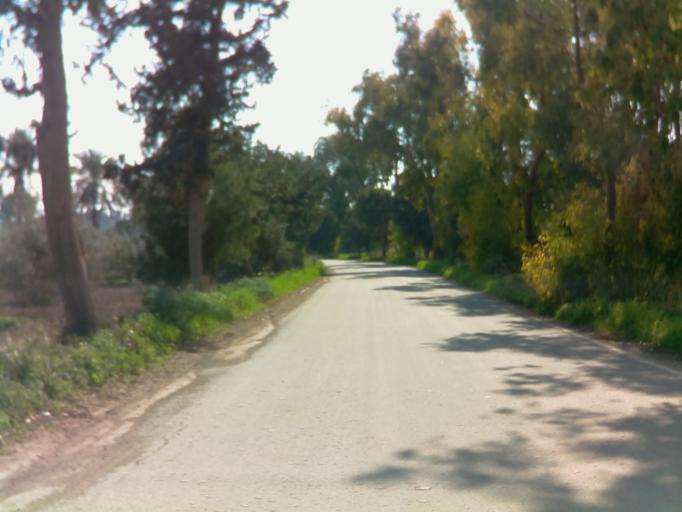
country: CY
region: Larnaka
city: Dhromolaxia
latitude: 34.8841
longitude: 33.6092
